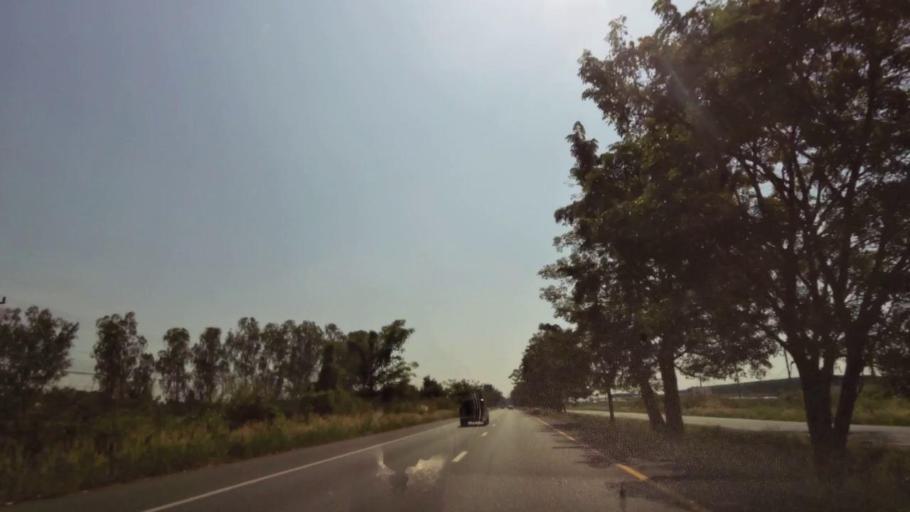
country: TH
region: Nakhon Sawan
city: Kao Liao
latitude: 15.9356
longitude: 100.1130
